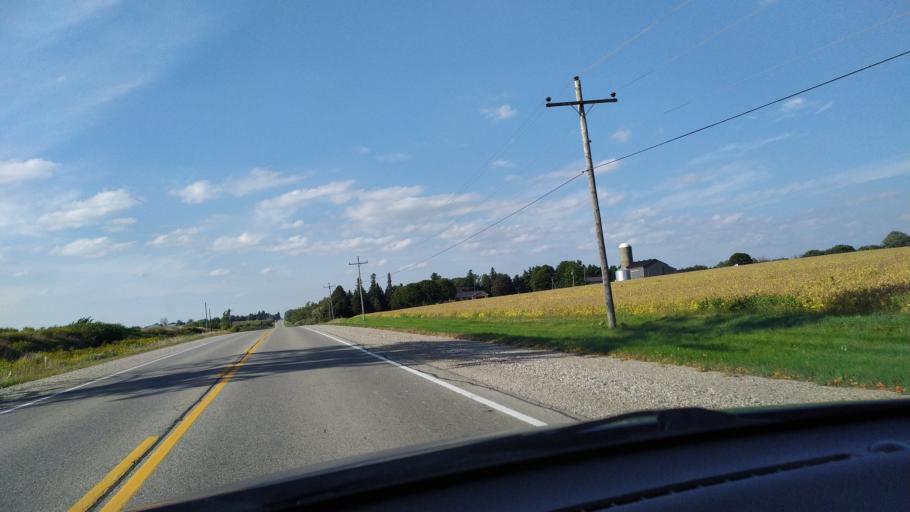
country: CA
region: Ontario
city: Ingersoll
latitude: 43.1342
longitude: -80.8903
